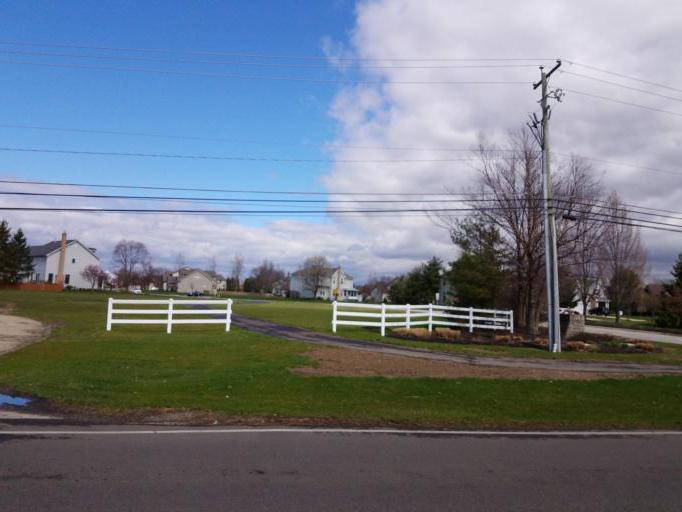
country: US
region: Ohio
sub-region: Franklin County
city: Westerville
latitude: 40.1452
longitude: -82.8892
